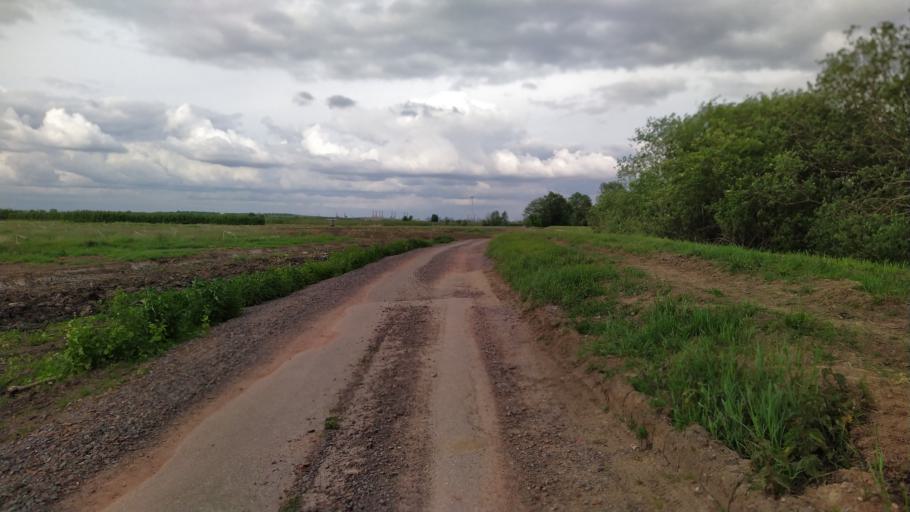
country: DE
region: Lower Saxony
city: Neu Wulmstorf
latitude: 53.4950
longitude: 9.8210
